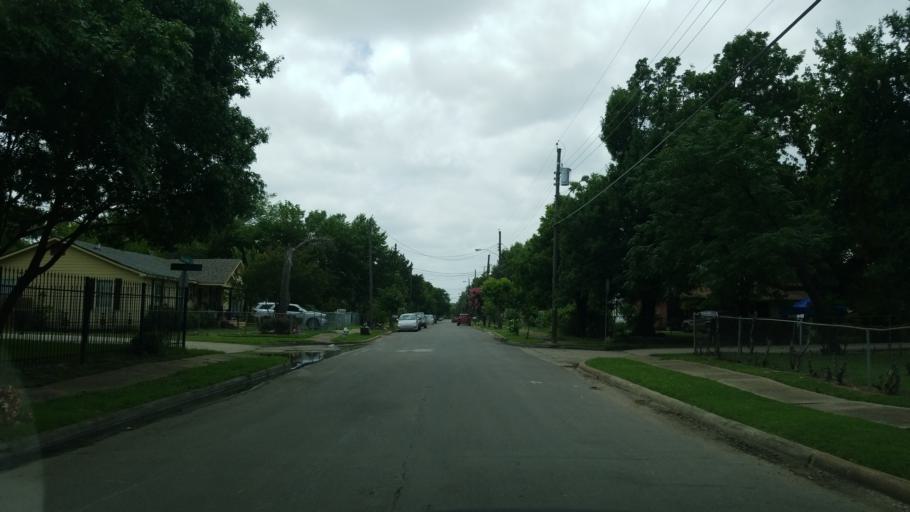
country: US
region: Texas
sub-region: Dallas County
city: Irving
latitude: 32.7874
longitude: -96.9036
